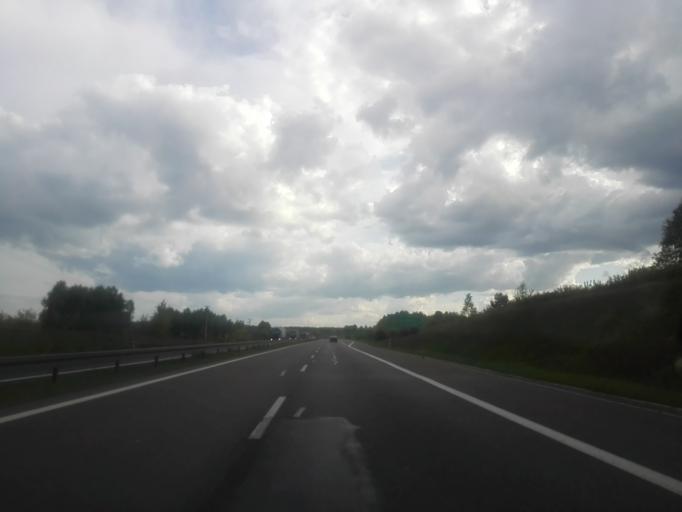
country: PL
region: Masovian Voivodeship
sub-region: Powiat ostrowski
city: Ostrow Mazowiecka
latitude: 52.8059
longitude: 21.8746
